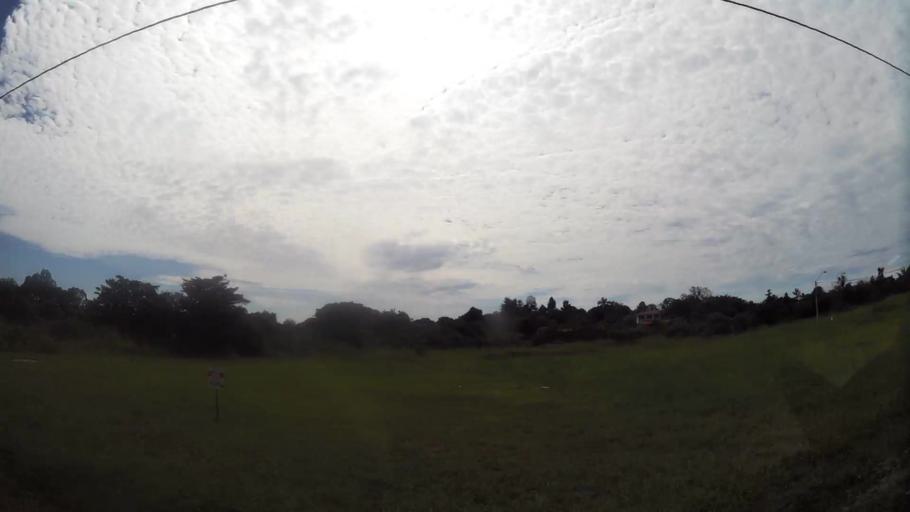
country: PA
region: Panama
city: Nueva Gorgona
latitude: 8.5377
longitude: -79.8959
